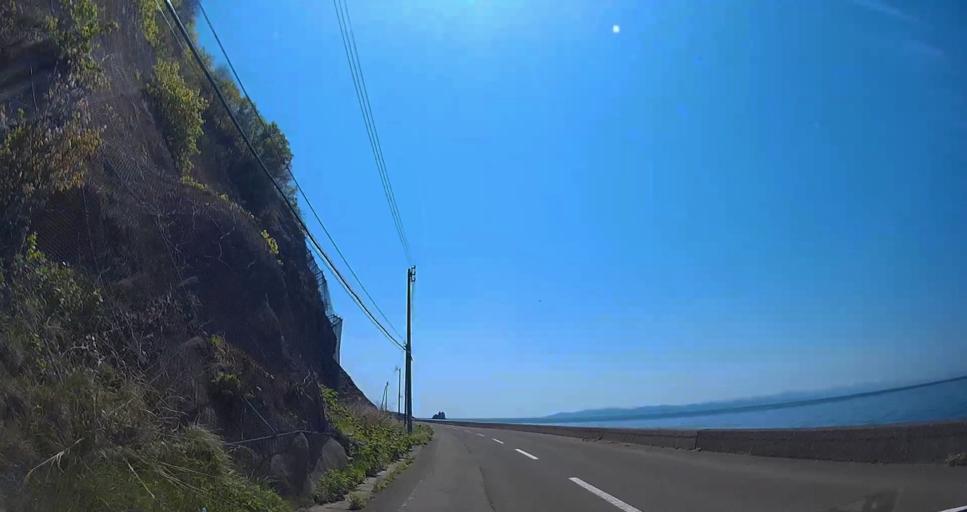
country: JP
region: Aomori
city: Aomori Shi
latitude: 41.1299
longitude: 140.7970
